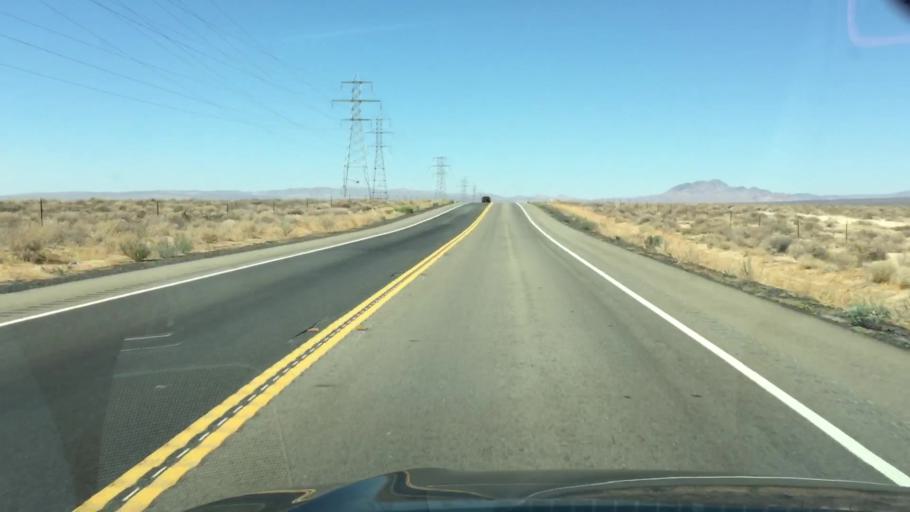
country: US
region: California
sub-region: Kern County
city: Boron
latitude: 35.1345
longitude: -117.5812
